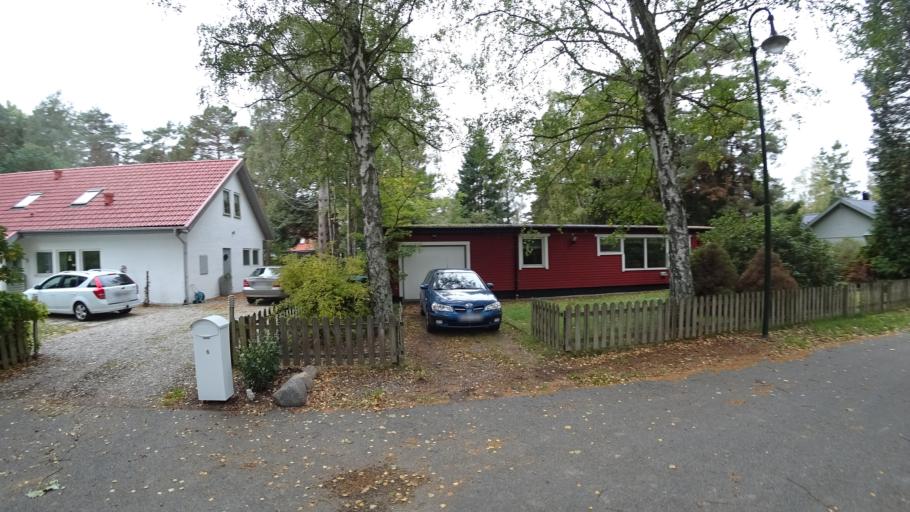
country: SE
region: Skane
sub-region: Kavlinge Kommun
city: Hofterup
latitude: 55.8156
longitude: 12.9804
